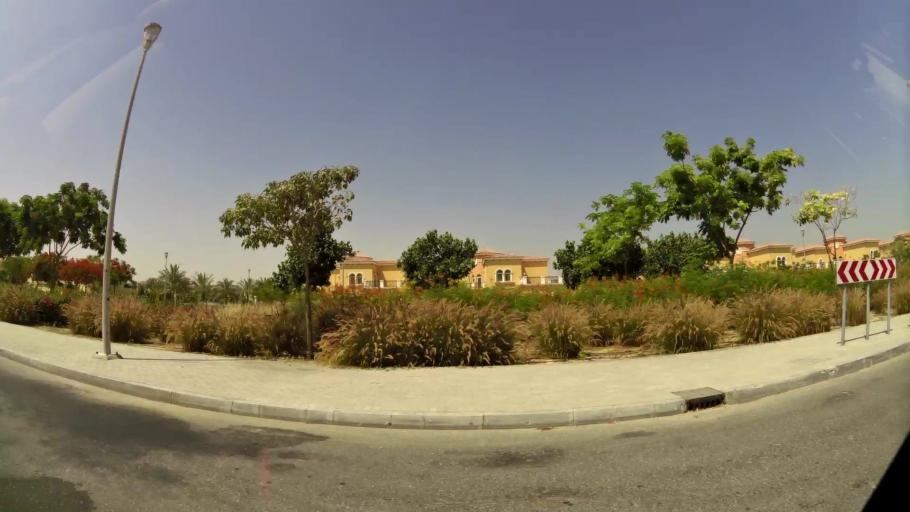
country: AE
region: Dubai
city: Dubai
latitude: 25.0532
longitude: 55.1484
